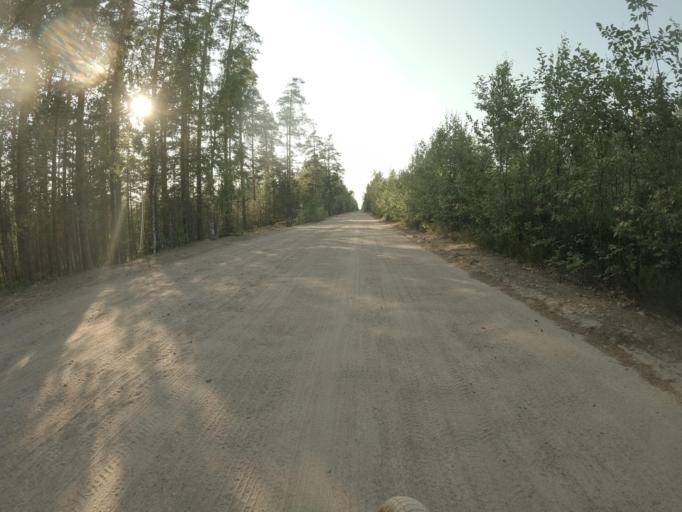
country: RU
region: Leningrad
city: Veshchevo
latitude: 60.4557
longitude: 29.2509
